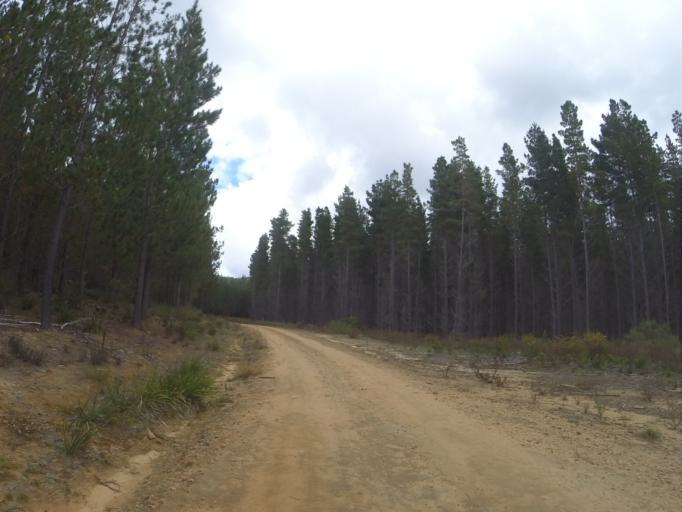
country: AU
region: New South Wales
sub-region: Wingecarribee
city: Moss Vale
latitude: -34.5188
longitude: 150.2480
